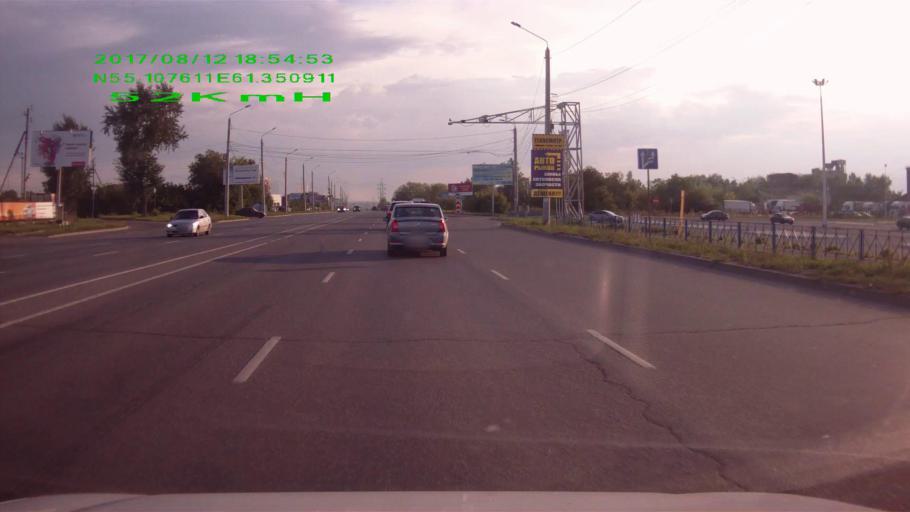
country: RU
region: Chelyabinsk
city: Novosineglazovskiy
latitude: 55.1025
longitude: 61.3433
